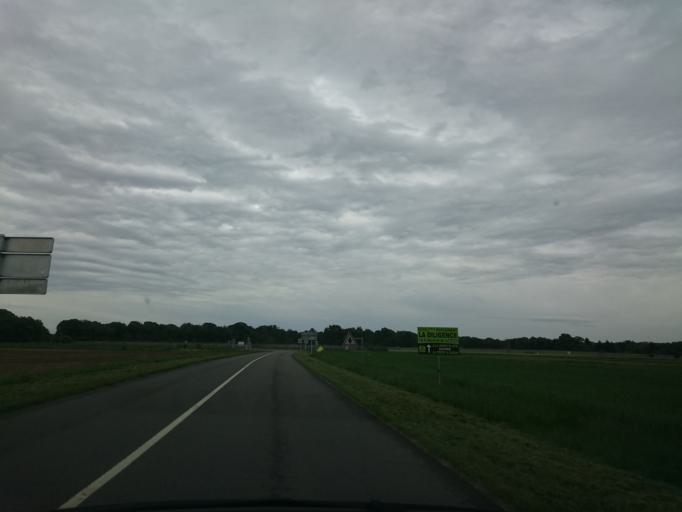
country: FR
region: Centre
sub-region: Departement du Loir-et-Cher
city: Muides-sur-Loire
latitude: 47.6620
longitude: 1.5346
